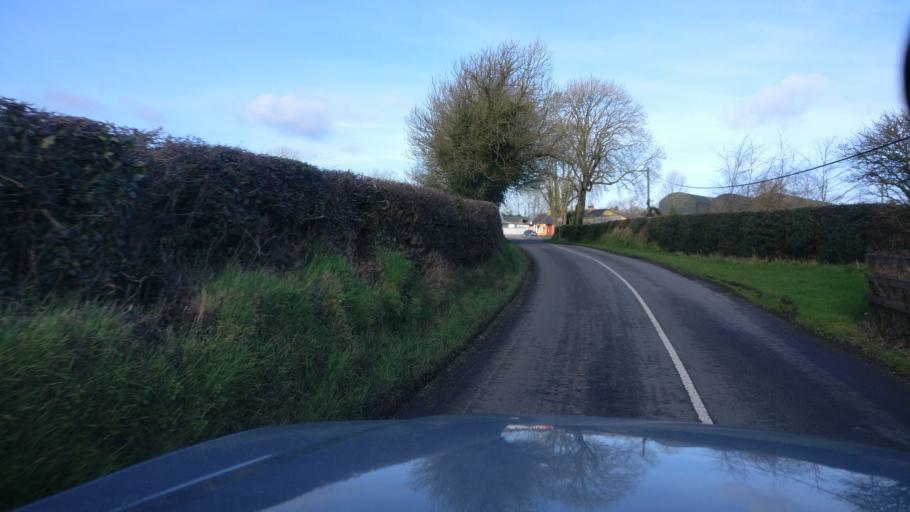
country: IE
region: Leinster
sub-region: Kilkenny
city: Castlecomer
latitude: 52.8877
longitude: -7.1609
